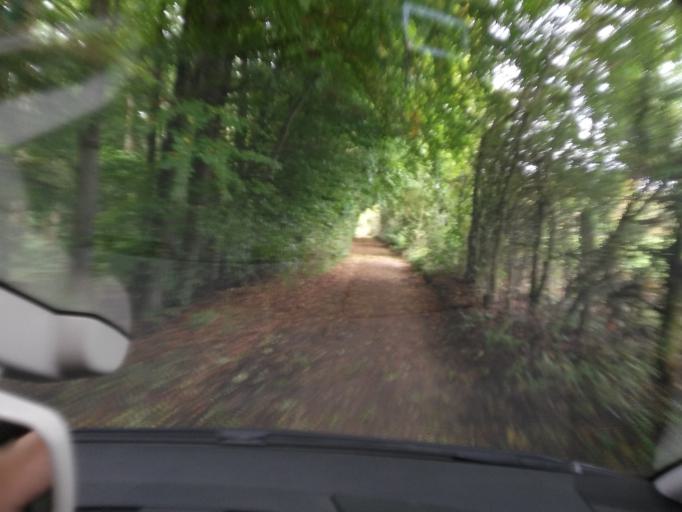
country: BE
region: Wallonia
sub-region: Province du Luxembourg
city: Attert
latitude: 49.7123
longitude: 5.7641
